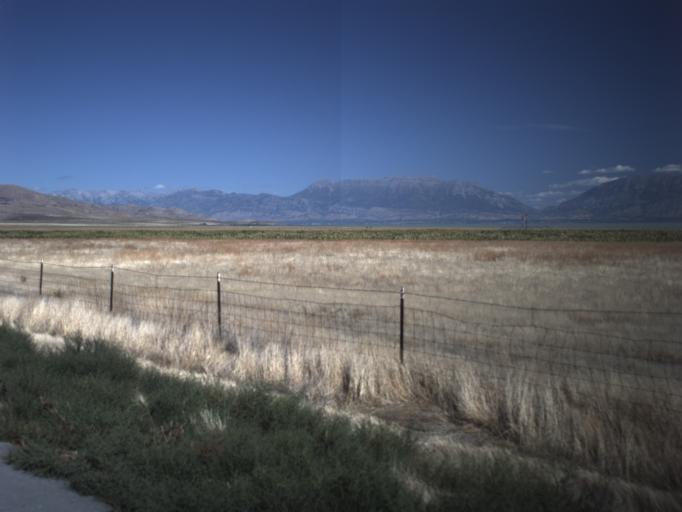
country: US
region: Utah
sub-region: Utah County
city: Genola
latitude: 40.1132
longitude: -111.9591
